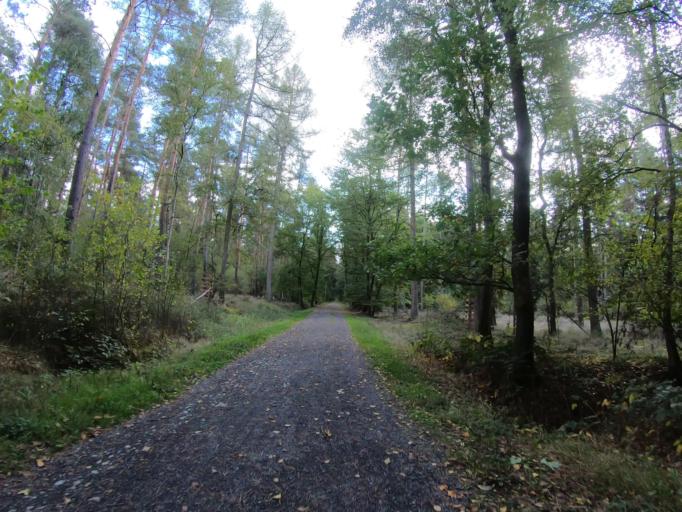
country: DE
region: Lower Saxony
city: Isenbuttel
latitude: 52.4516
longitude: 10.5728
